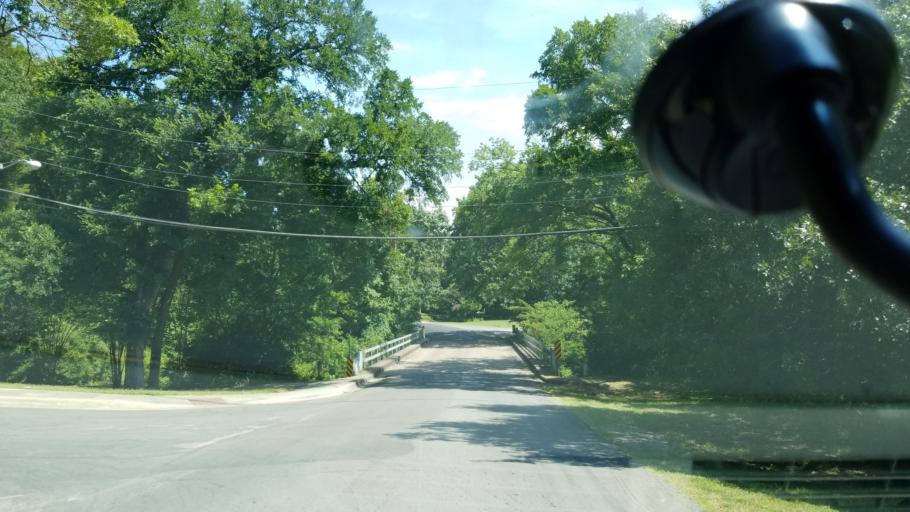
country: US
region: Texas
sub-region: Dallas County
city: Cockrell Hill
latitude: 32.7074
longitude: -96.8810
